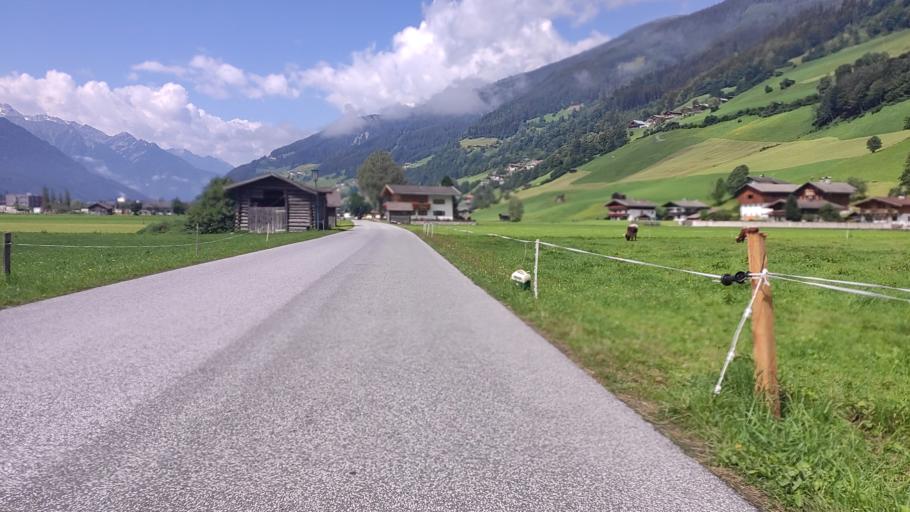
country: AT
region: Salzburg
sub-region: Politischer Bezirk Zell am See
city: Bramberg am Wildkogel
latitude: 47.2773
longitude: 12.3655
